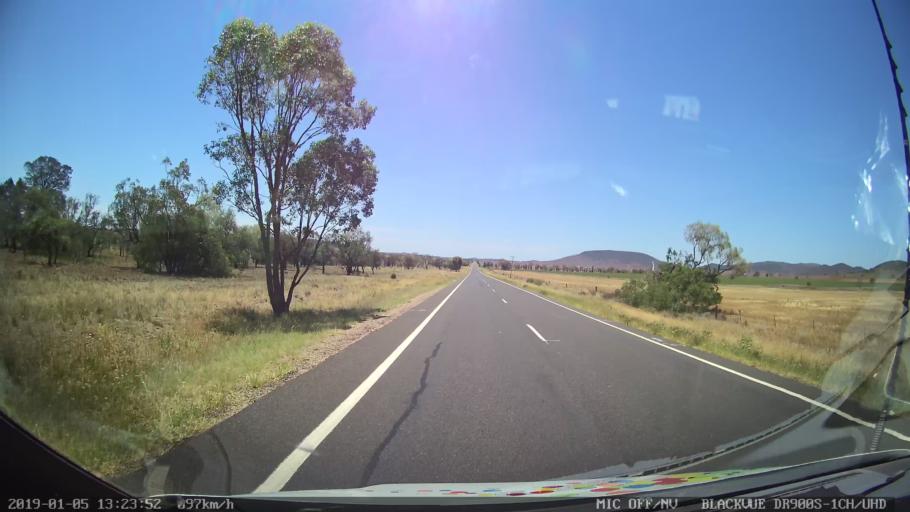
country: AU
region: New South Wales
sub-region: Gunnedah
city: Gunnedah
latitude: -31.0743
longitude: 149.9811
